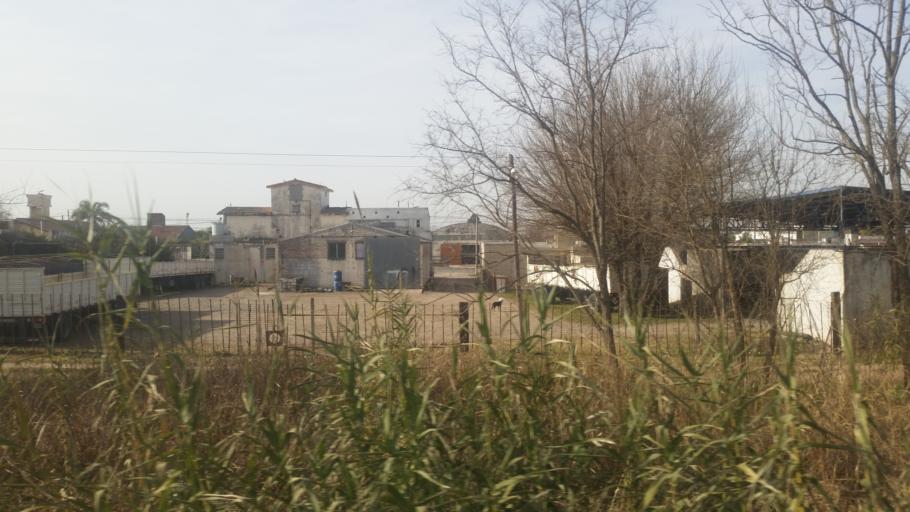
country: AR
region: Cordoba
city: Laguna Larga
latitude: -31.7828
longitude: -63.7978
